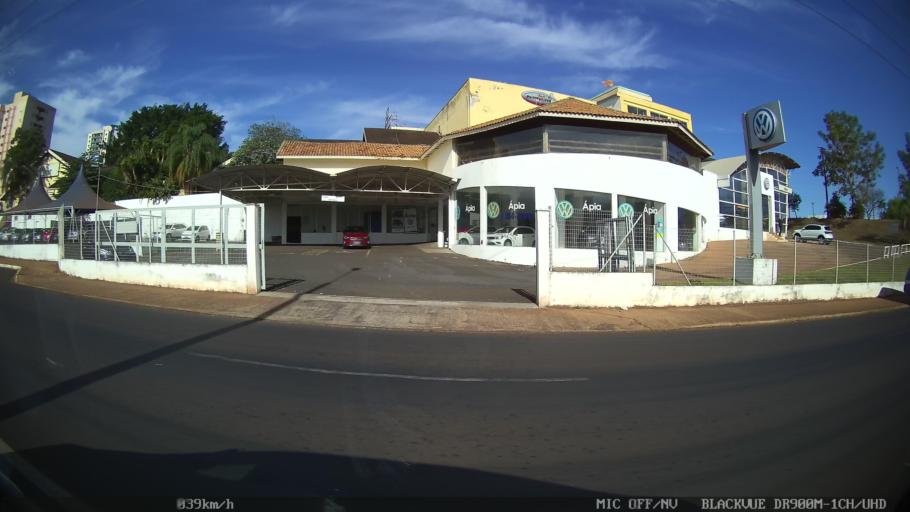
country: BR
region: Sao Paulo
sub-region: Araraquara
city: Araraquara
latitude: -21.8068
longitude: -48.1725
